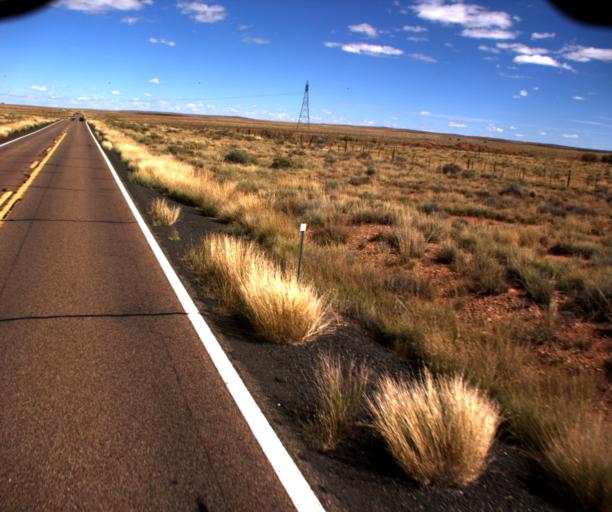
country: US
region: Arizona
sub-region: Navajo County
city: Holbrook
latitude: 34.7901
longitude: -110.2209
